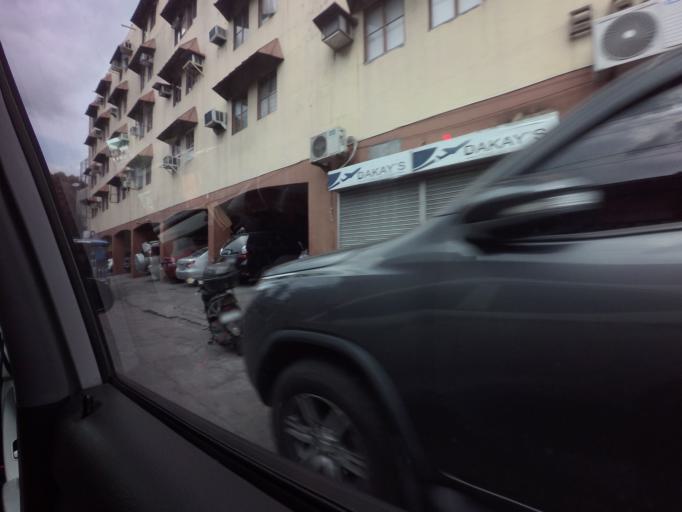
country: PH
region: Metro Manila
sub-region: City of Manila
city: Quiapo
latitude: 14.6043
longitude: 121.0062
